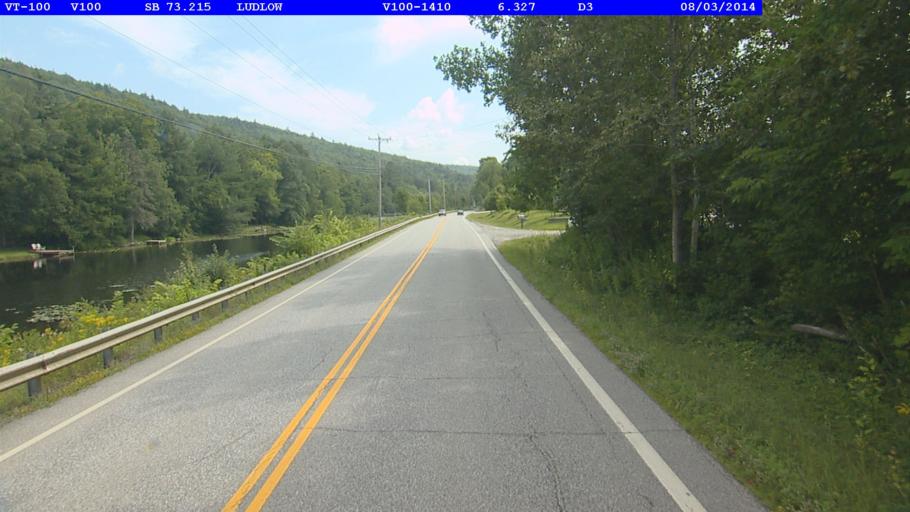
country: US
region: Vermont
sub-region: Windsor County
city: Chester
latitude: 43.4364
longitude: -72.6987
